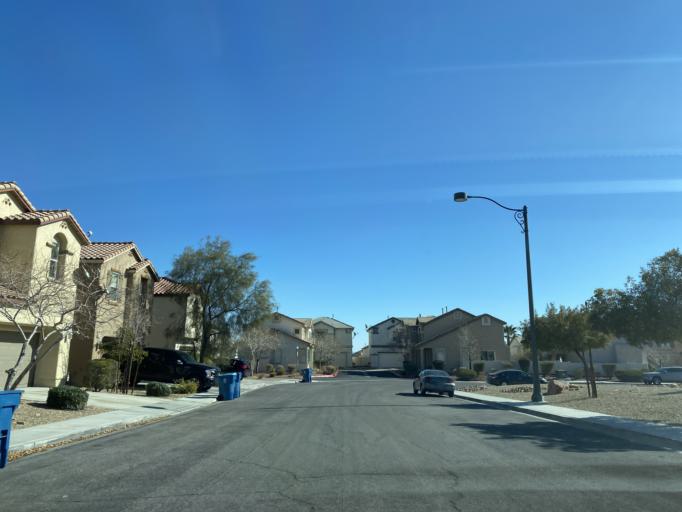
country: US
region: Nevada
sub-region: Clark County
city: Summerlin South
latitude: 36.2860
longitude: -115.2952
